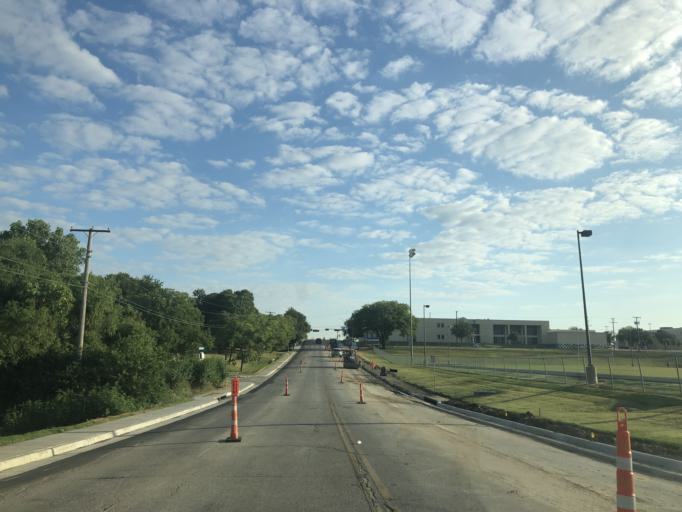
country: US
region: Texas
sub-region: Dallas County
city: Grand Prairie
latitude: 32.7510
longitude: -97.0058
